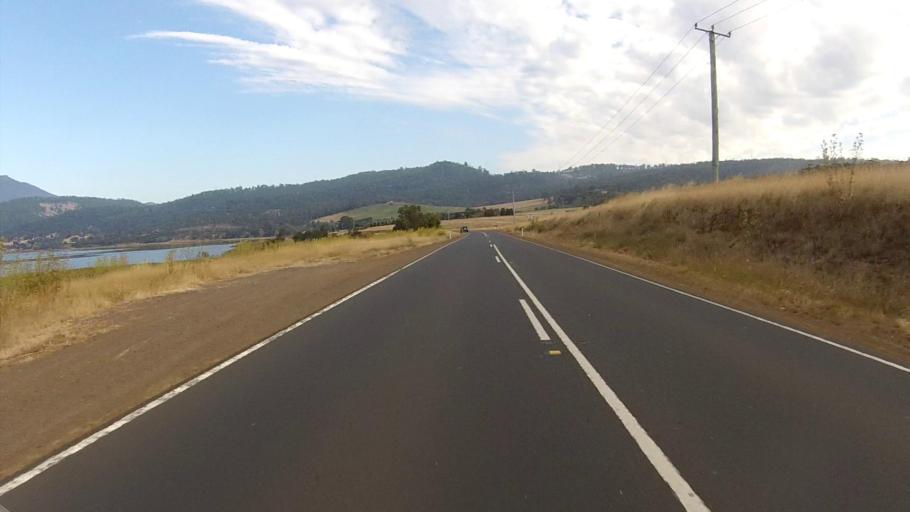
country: AU
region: Tasmania
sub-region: Brighton
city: Bridgewater
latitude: -42.7324
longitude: 147.2109
